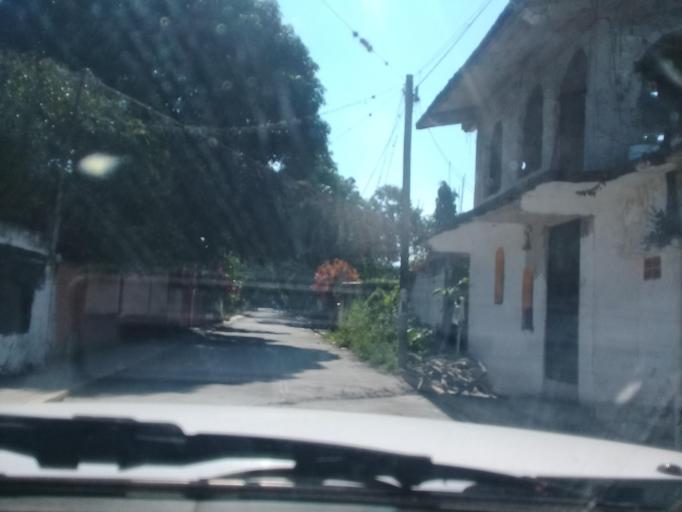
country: MX
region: Veracruz
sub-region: Emiliano Zapata
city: Plan del Rio
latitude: 19.4159
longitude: -96.6175
